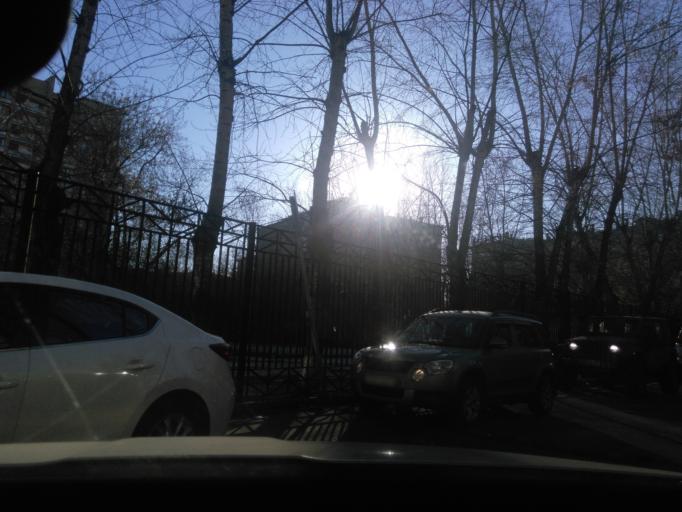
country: RU
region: Moskovskaya
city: Koptevo
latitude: 55.8171
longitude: 37.5043
